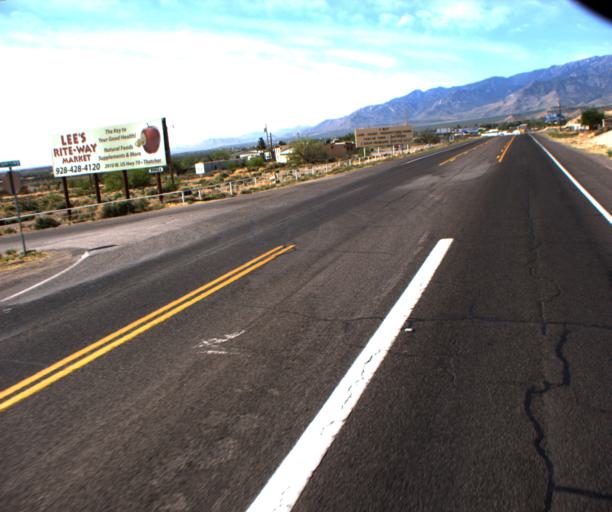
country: US
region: Arizona
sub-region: Graham County
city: Cactus Flat
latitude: 32.7844
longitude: -109.7127
